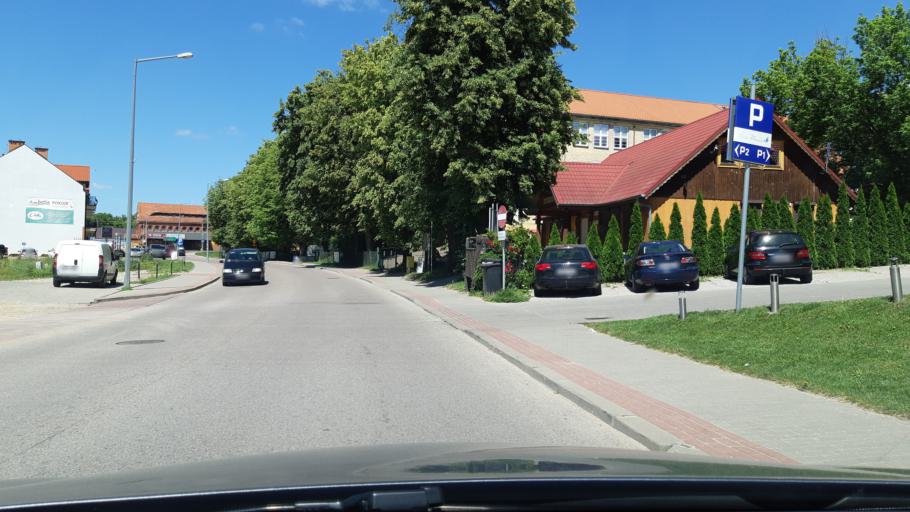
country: PL
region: Warmian-Masurian Voivodeship
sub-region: Powiat mragowski
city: Mikolajki
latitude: 53.8030
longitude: 21.5743
